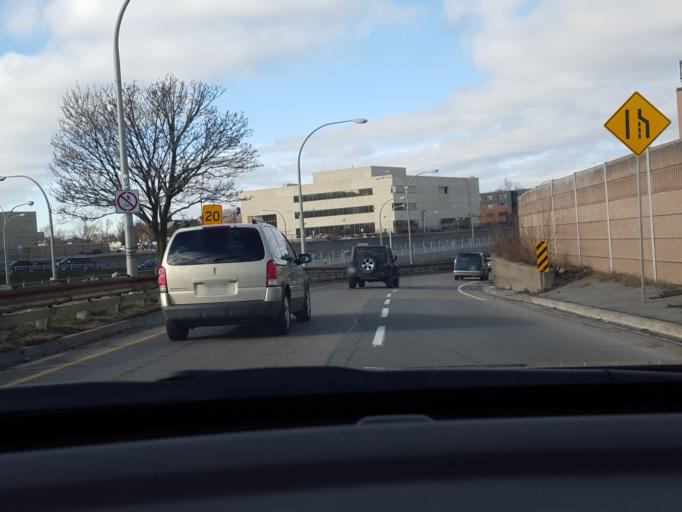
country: CA
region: Ontario
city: Toronto
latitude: 43.7166
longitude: -79.4437
